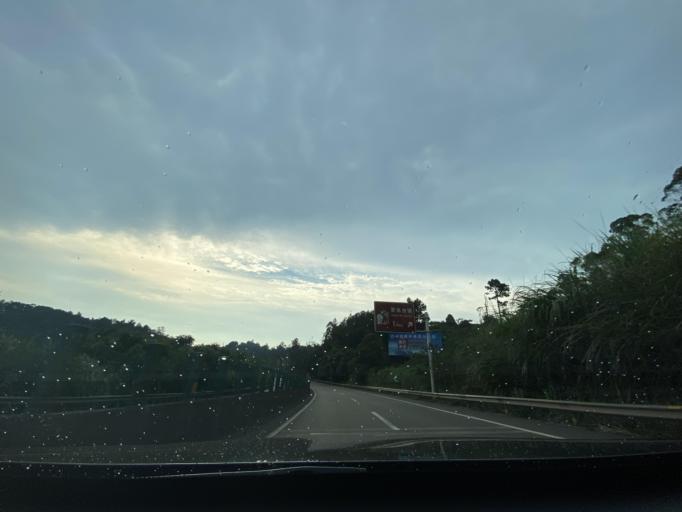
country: CN
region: Sichuan
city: Chonglong
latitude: 29.7972
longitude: 104.7228
